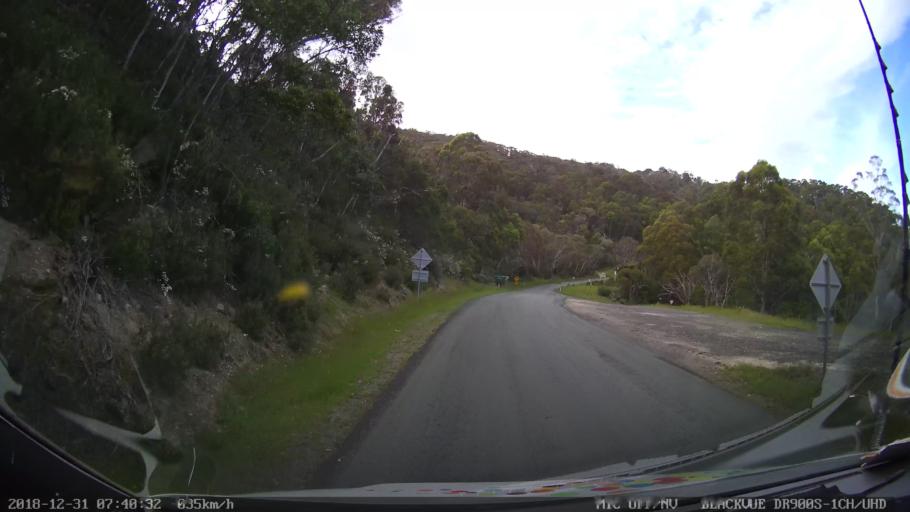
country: AU
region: New South Wales
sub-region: Snowy River
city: Jindabyne
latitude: -36.3510
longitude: 148.4163
